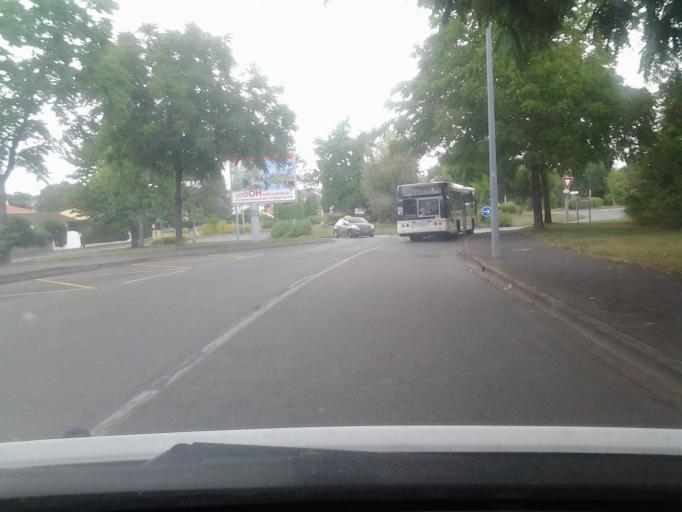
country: FR
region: Pays de la Loire
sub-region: Departement de la Vendee
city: La Roche-sur-Yon
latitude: 46.6603
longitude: -1.4267
